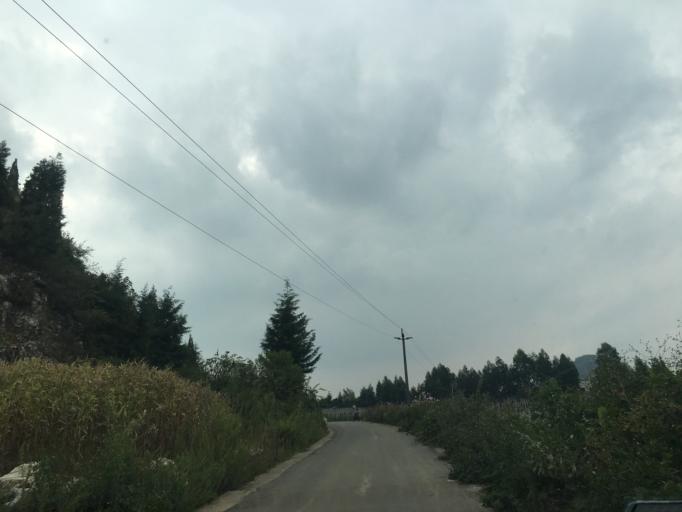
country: CN
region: Guangxi Zhuangzu Zizhiqu
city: Xinzhou
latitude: 25.4837
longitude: 105.6458
